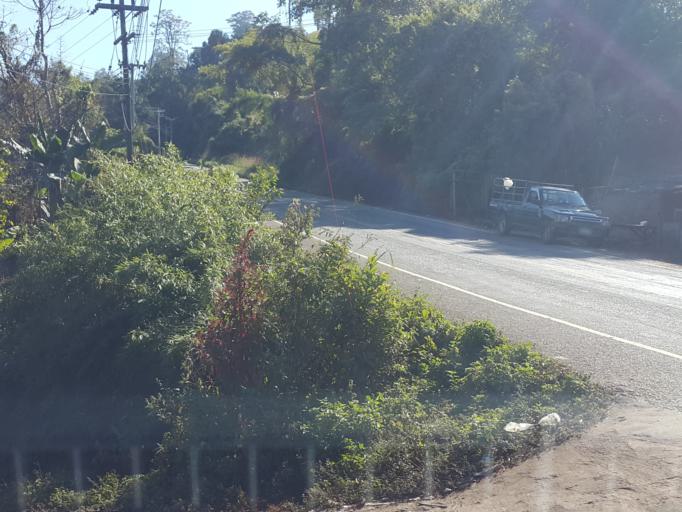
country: TH
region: Chiang Mai
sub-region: Amphoe Chiang Dao
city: Chiang Dao
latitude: 19.5250
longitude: 98.8621
